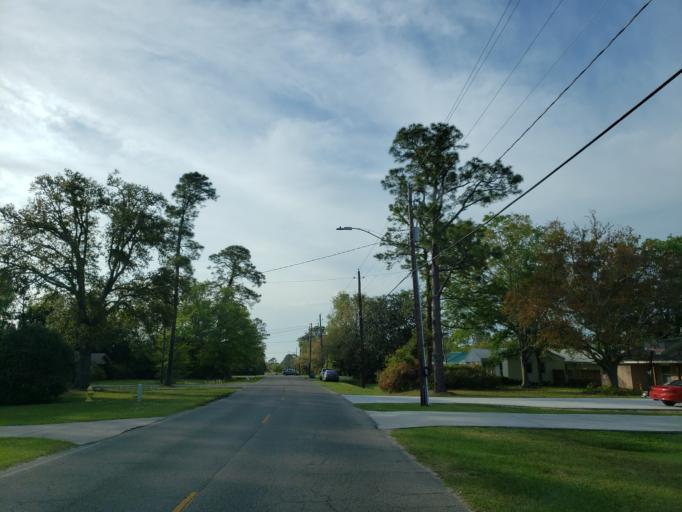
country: US
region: Mississippi
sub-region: Harrison County
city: West Gulfport
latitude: 30.4130
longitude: -89.0555
